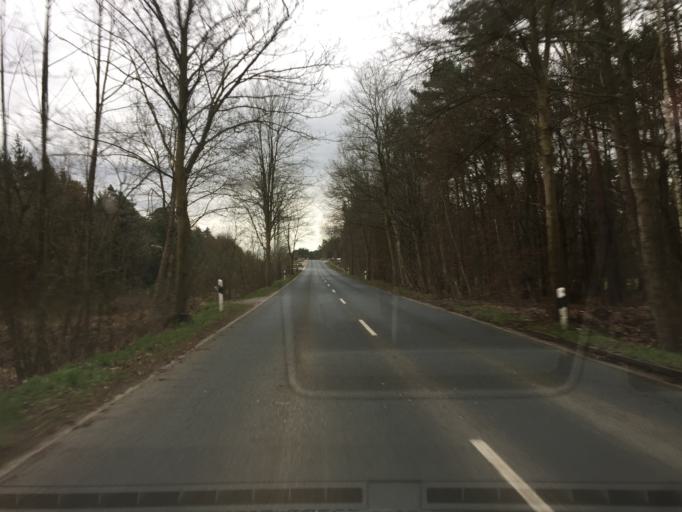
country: DE
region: Lower Saxony
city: Neustadt am Rubenberge
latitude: 52.4892
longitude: 9.4915
